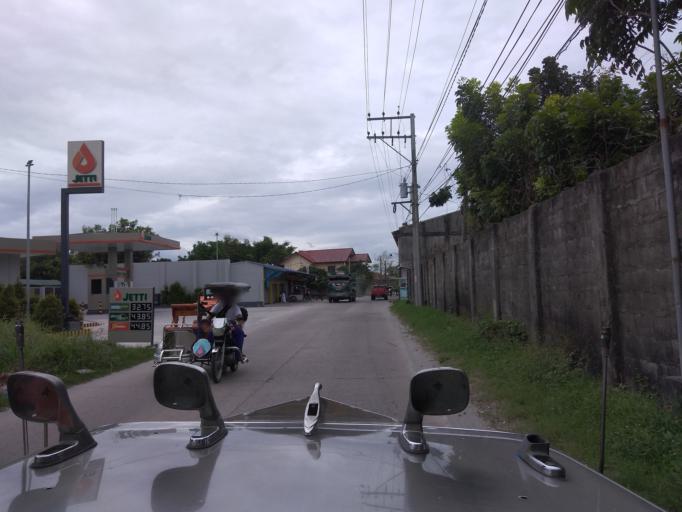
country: PH
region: Central Luzon
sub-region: Province of Pampanga
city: Pandacaqui
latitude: 15.1875
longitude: 120.6389
